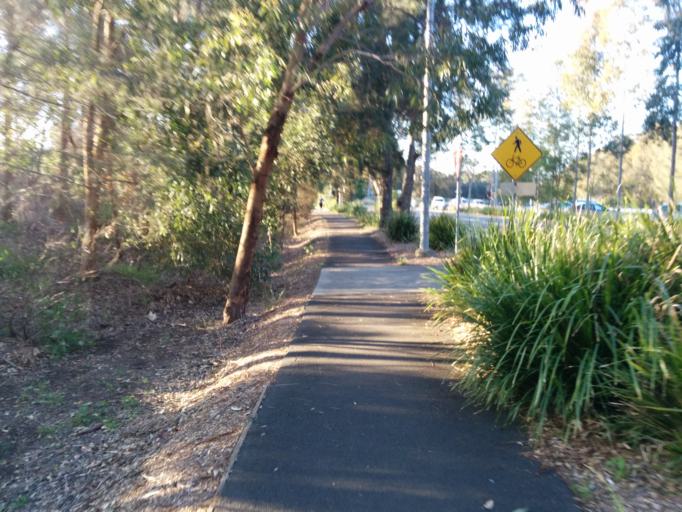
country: AU
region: New South Wales
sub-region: Canada Bay
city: Concord West
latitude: -33.8413
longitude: 151.0761
